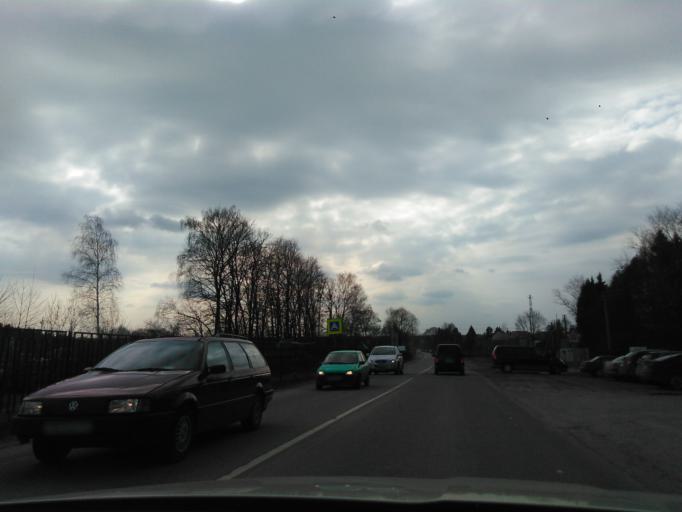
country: RU
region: Moskovskaya
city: Marfino
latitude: 56.0546
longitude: 37.5294
